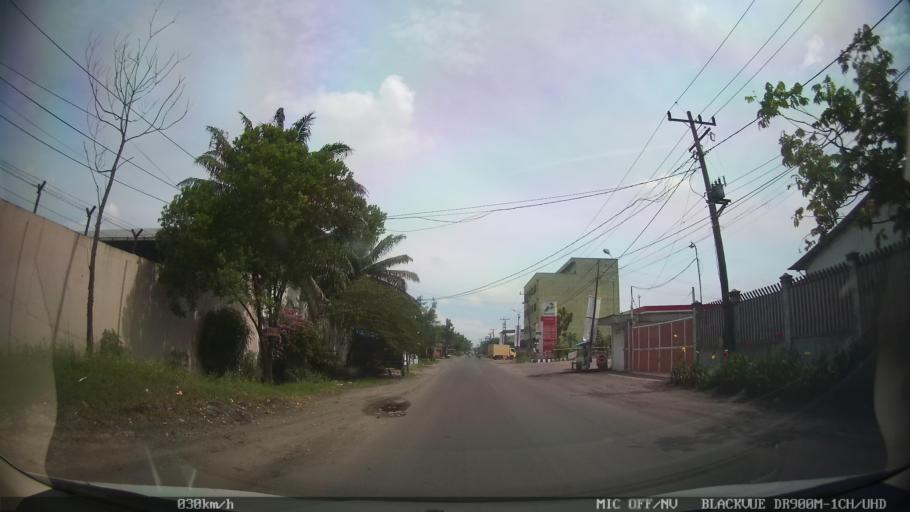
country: ID
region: North Sumatra
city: Medan
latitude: 3.6389
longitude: 98.7165
